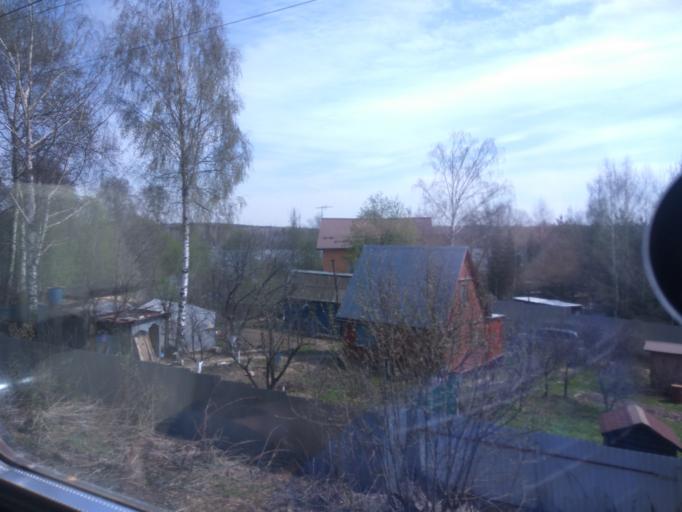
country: RU
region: Moskovskaya
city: Yermolino
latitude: 56.1450
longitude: 37.5069
